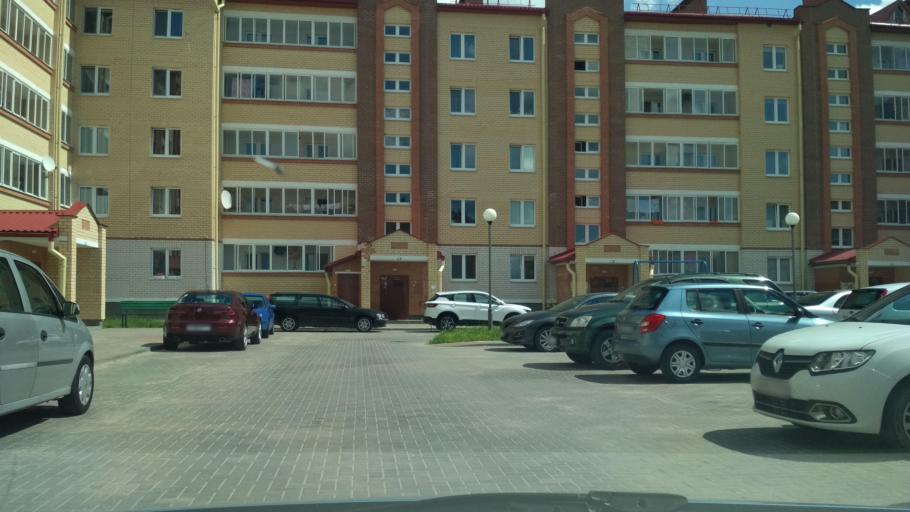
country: BY
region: Grodnenskaya
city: Astravyets
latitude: 54.6084
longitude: 25.9667
